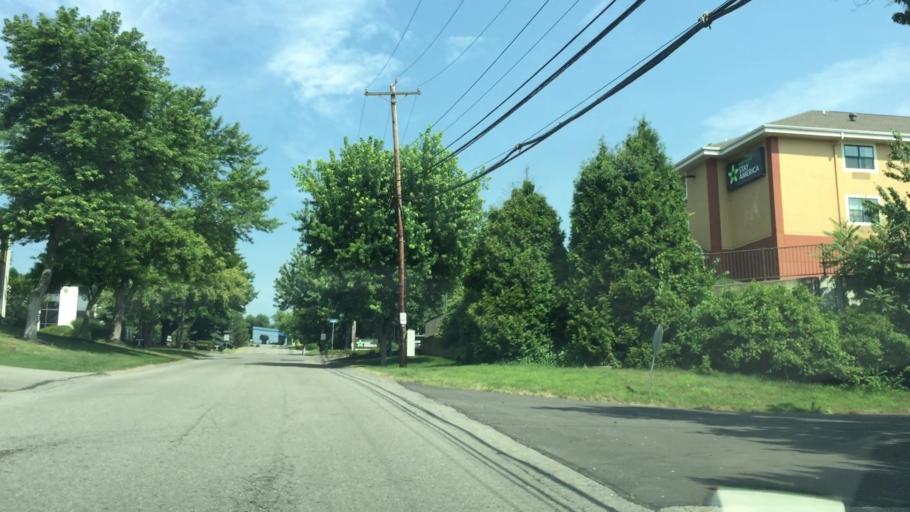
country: US
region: Pennsylvania
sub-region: Allegheny County
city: Carnegie
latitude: 40.4166
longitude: -80.0884
